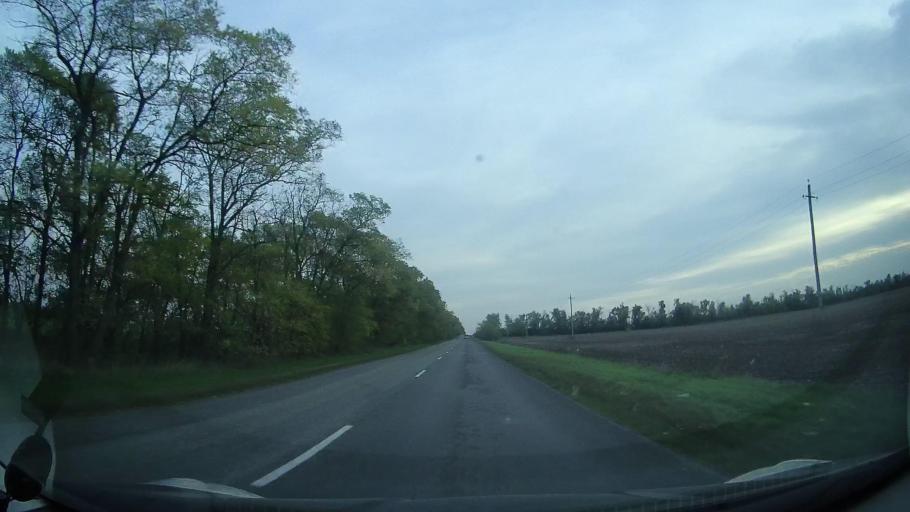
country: RU
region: Rostov
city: Ol'ginskaya
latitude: 47.1016
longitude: 39.9775
